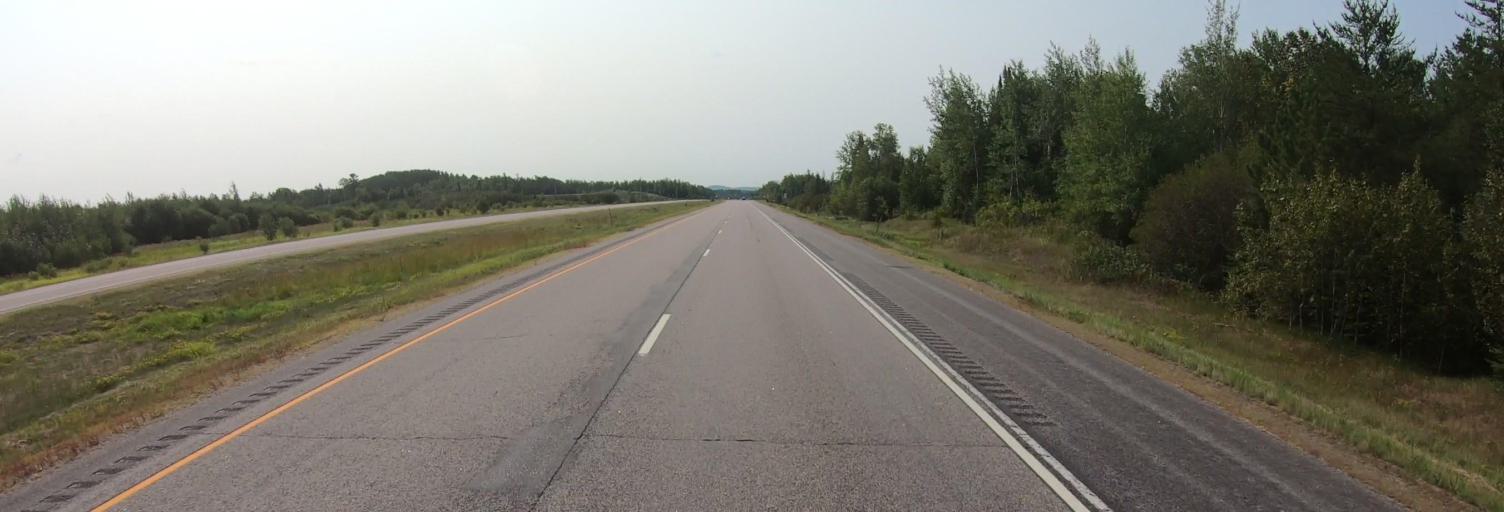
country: US
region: Minnesota
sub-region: Saint Louis County
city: Parkville
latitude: 47.6468
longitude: -92.5665
